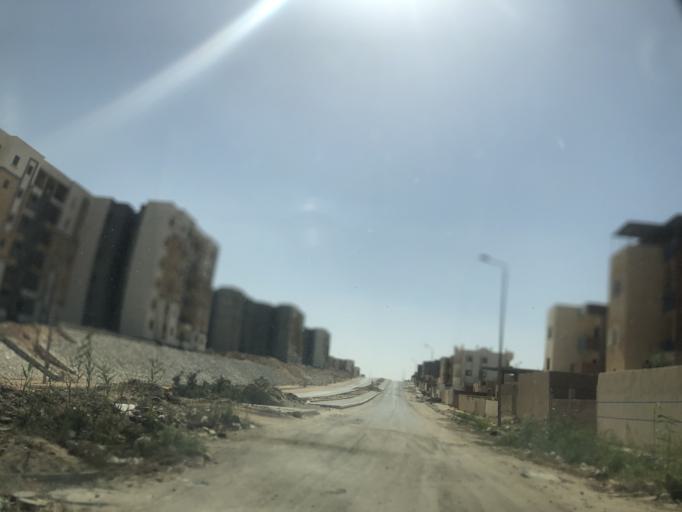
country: EG
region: Al Jizah
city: Madinat Sittah Uktubar
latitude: 29.9289
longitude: 31.0067
